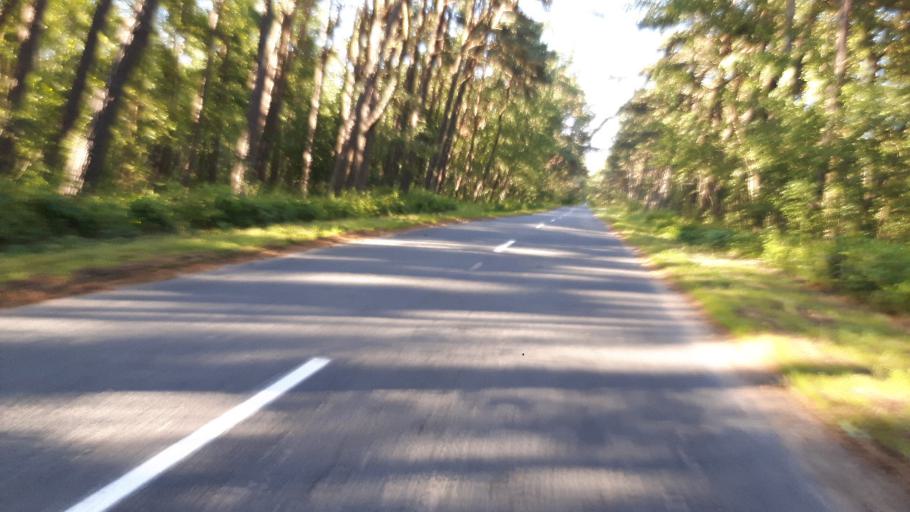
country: LT
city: Nida
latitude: 55.2443
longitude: 20.9189
